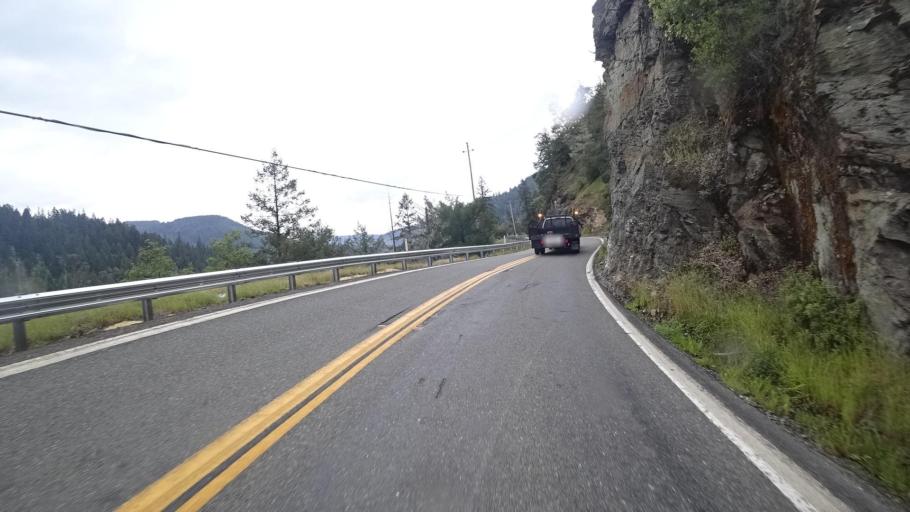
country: US
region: California
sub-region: Humboldt County
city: Willow Creek
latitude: 41.1206
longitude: -123.6883
